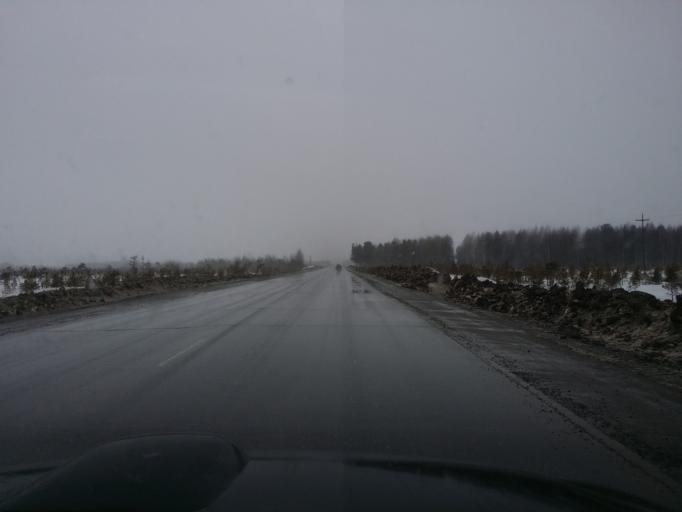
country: RU
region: Khanty-Mansiyskiy Avtonomnyy Okrug
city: Nizhnevartovsk
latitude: 60.9586
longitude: 76.7321
